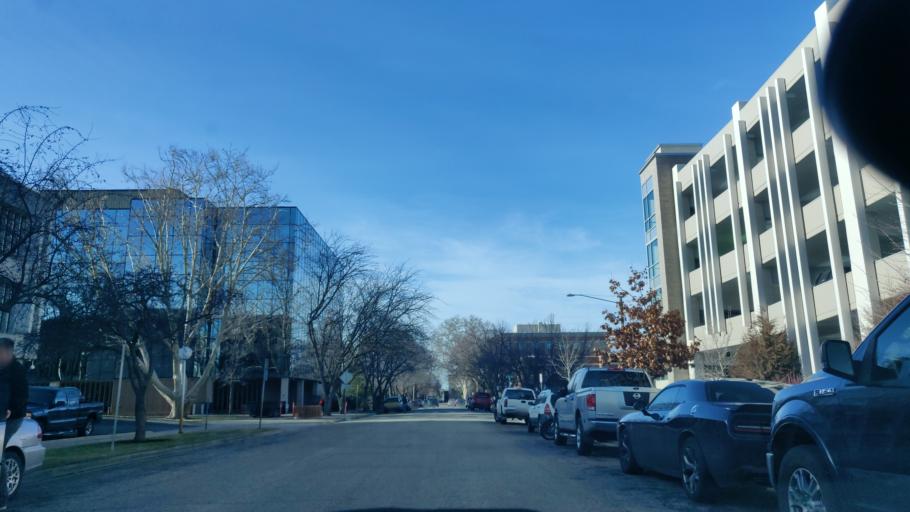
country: US
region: Idaho
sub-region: Ada County
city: Boise
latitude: 43.6186
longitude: -116.1980
